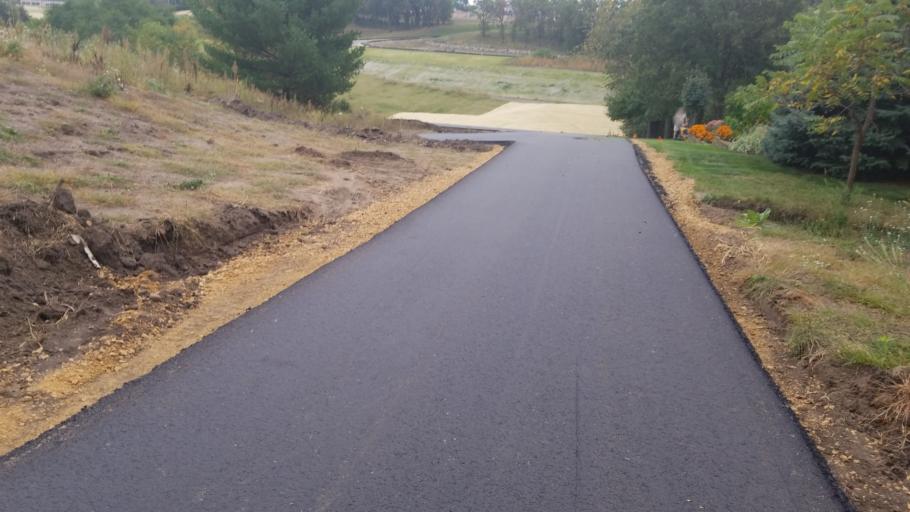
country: US
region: Wisconsin
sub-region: Saint Croix County
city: Hudson
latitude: 44.9716
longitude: -92.7311
